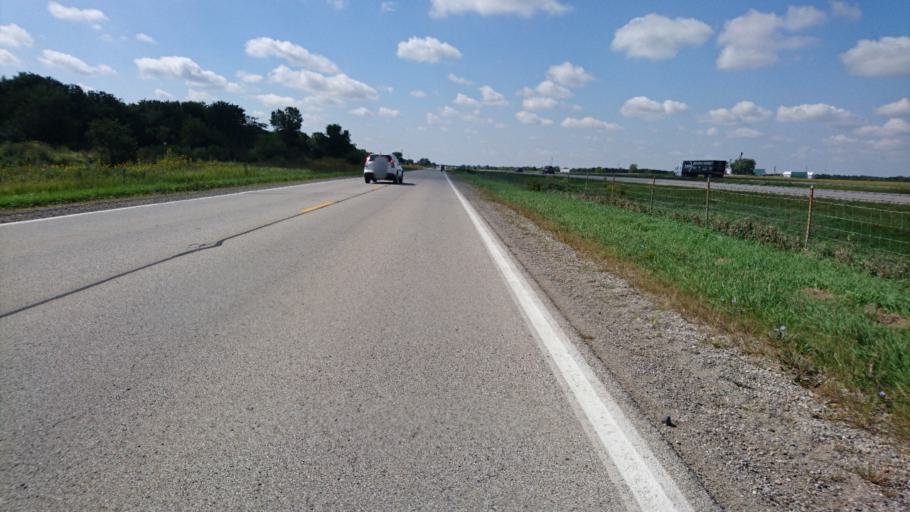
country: US
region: Illinois
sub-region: McLean County
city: Lexington
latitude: 40.6131
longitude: -88.8269
